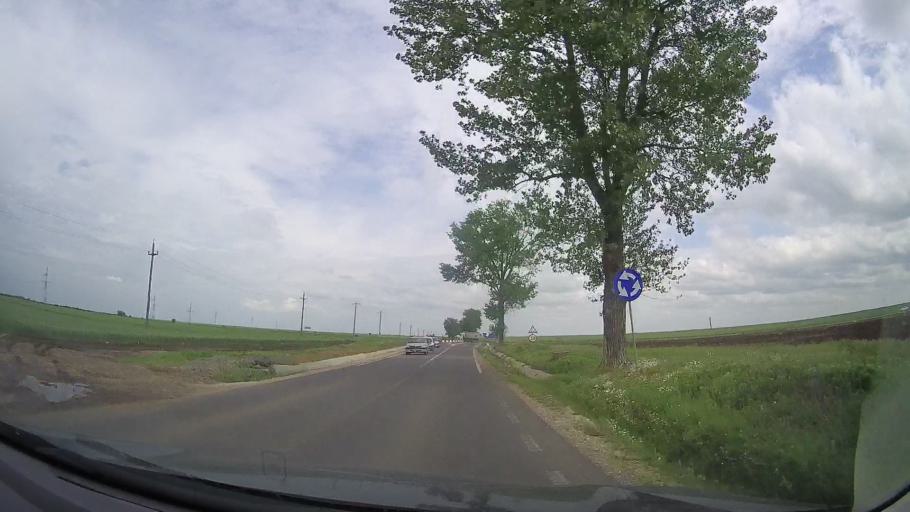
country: RO
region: Teleorman
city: Alexandria
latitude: 43.9892
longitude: 25.3466
